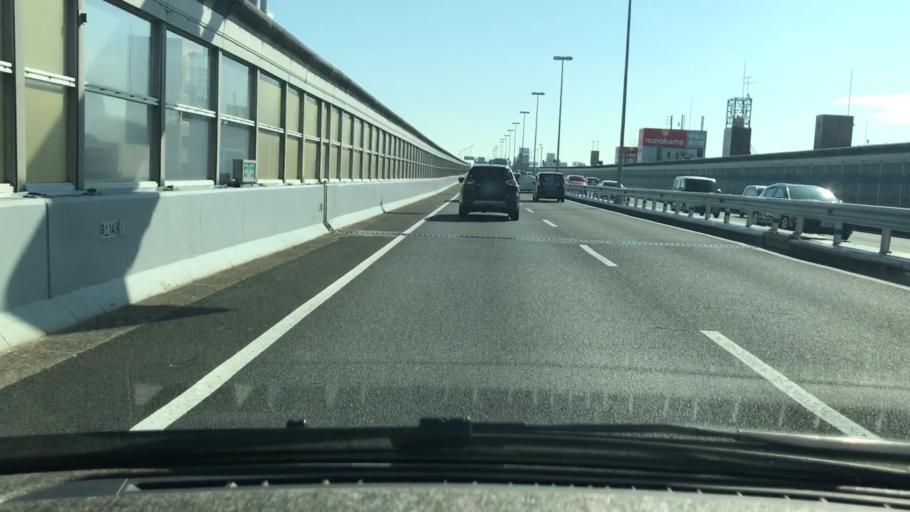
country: JP
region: Hyogo
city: Nishinomiya-hama
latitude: 34.7301
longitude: 135.3500
